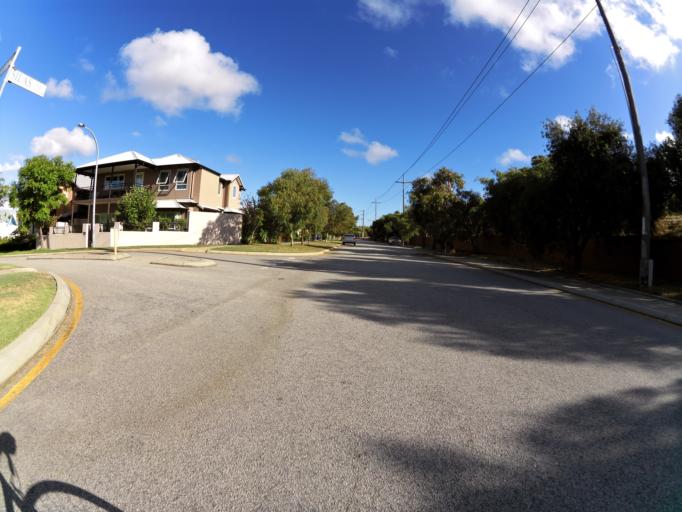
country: AU
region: Western Australia
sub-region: Fremantle
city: Fremantle
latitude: -32.0455
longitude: 115.7644
